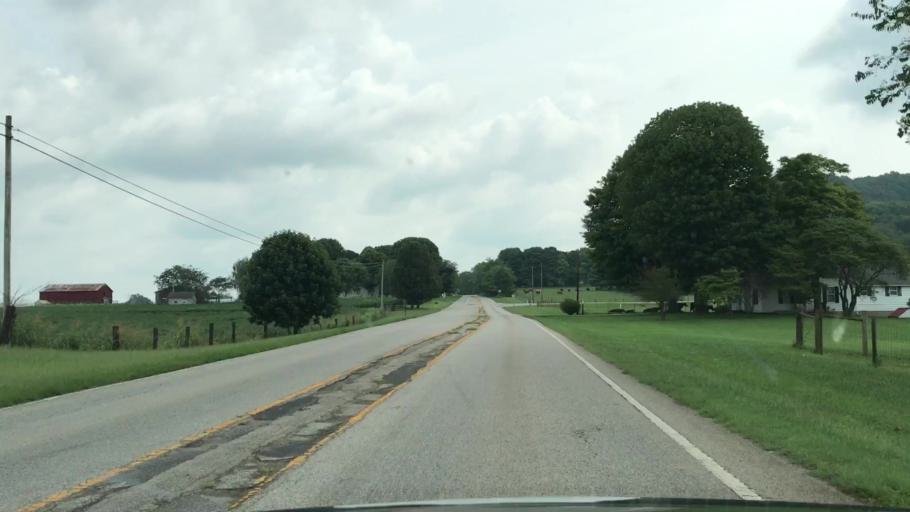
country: US
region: Kentucky
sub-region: Barren County
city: Cave City
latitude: 37.1114
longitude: -85.9899
